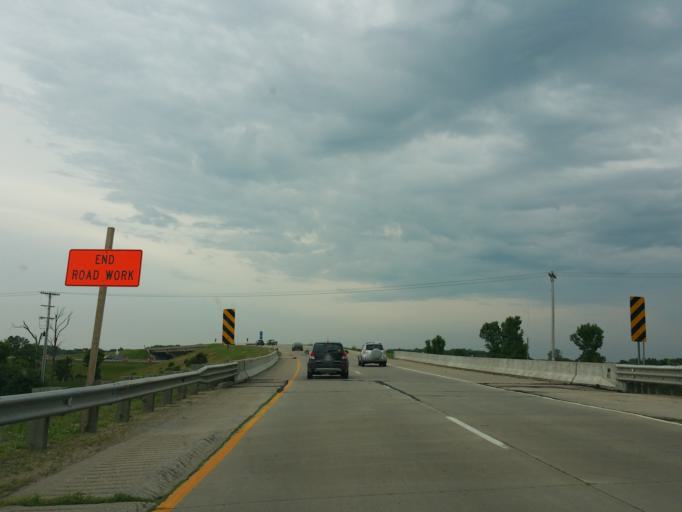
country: US
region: Wisconsin
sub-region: Dane County
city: Monona
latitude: 43.1070
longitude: -89.2846
